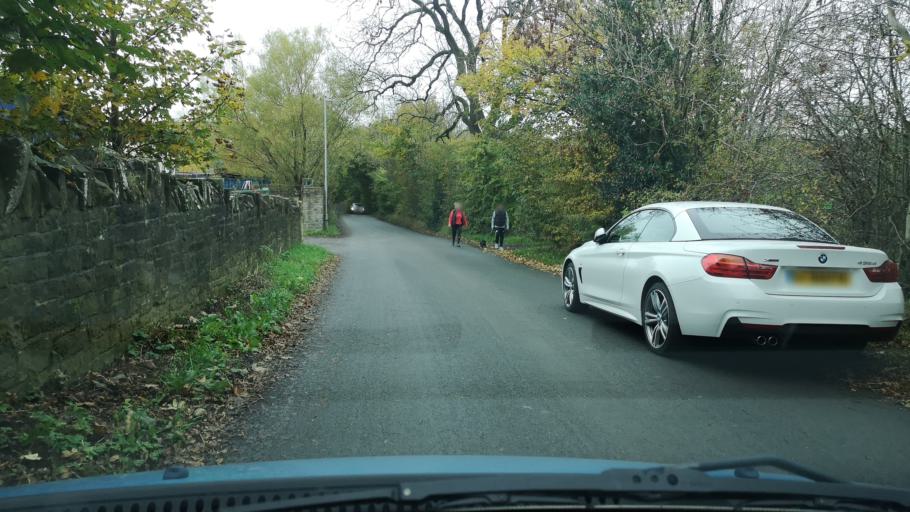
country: GB
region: England
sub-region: City and Borough of Leeds
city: Drighlington
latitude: 53.7383
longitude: -1.6734
